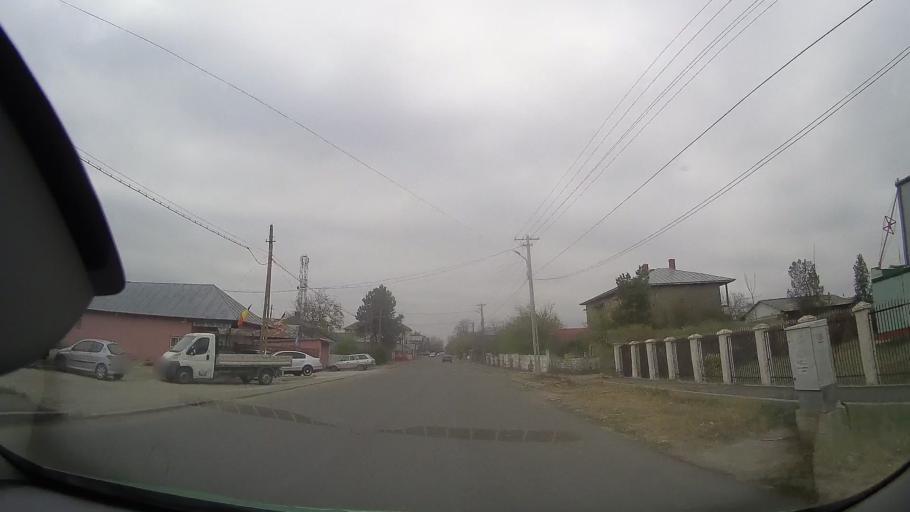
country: RO
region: Buzau
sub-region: Comuna Pogoanele
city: Pogoanele
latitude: 44.9188
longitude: 26.9918
